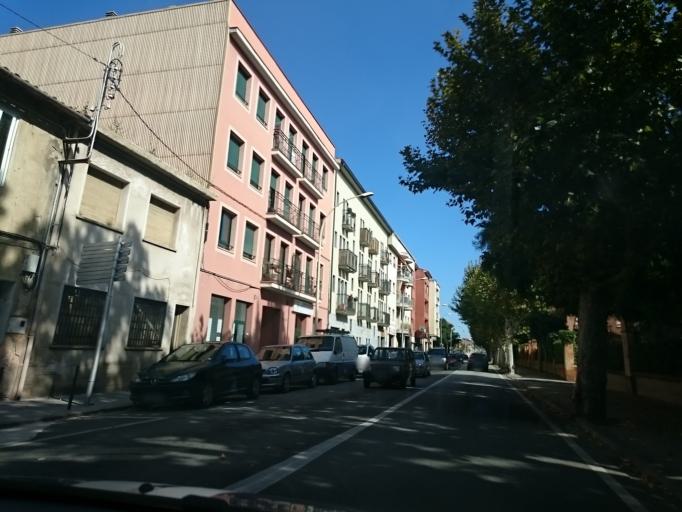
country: ES
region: Catalonia
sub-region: Provincia de Barcelona
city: Cardedeu
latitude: 41.6373
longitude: 2.3622
